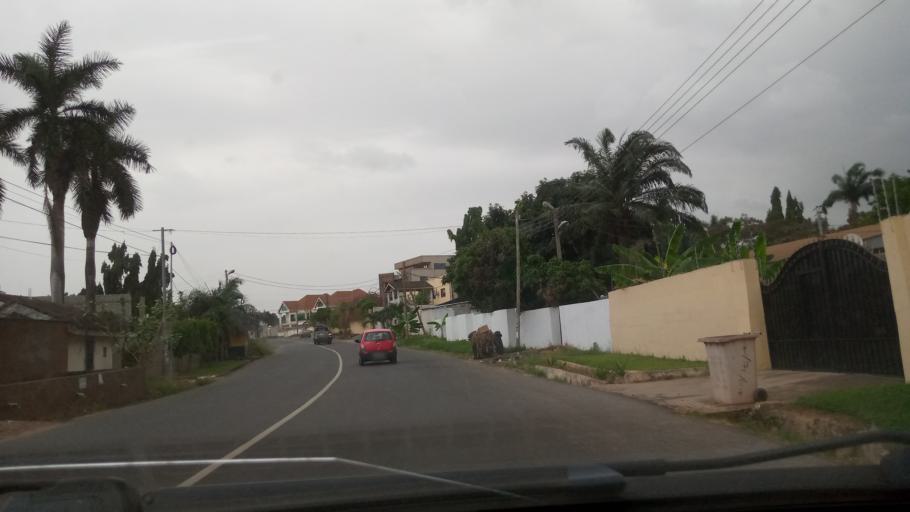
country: GH
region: Greater Accra
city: Dome
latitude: 5.6156
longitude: -0.2018
